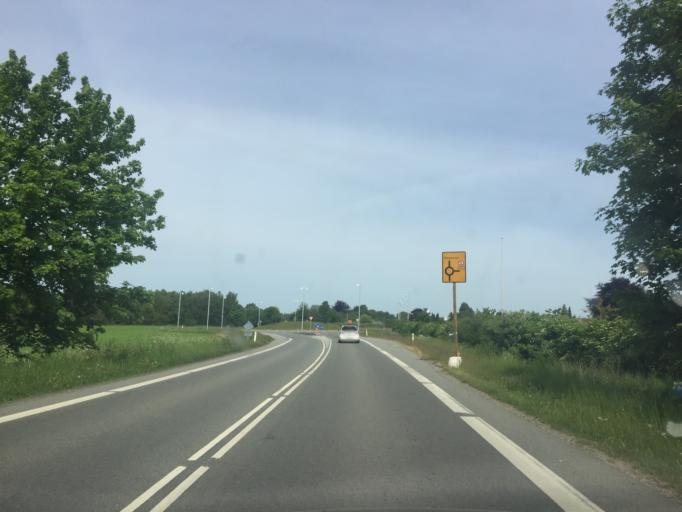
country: DK
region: South Denmark
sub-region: Nyborg Kommune
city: Nyborg
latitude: 55.3042
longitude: 10.7251
